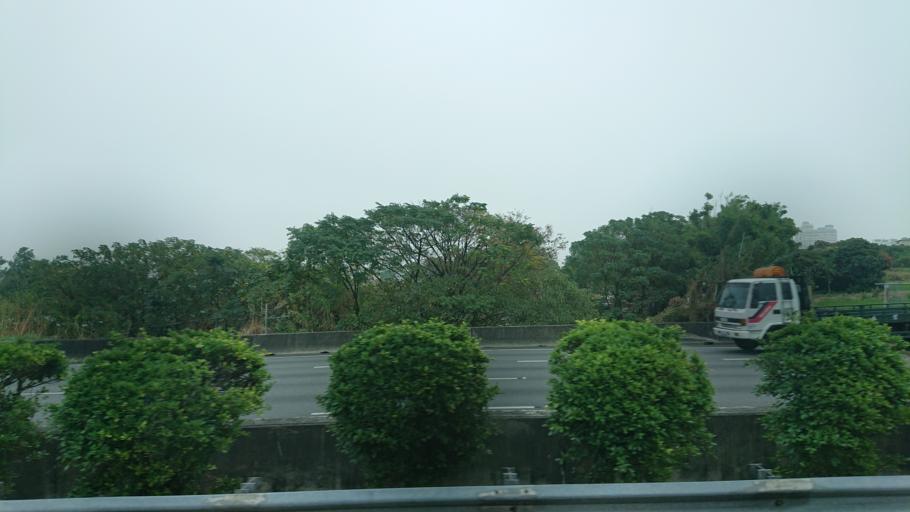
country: TW
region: Taiwan
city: Fengyuan
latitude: 24.2575
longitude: 120.6913
